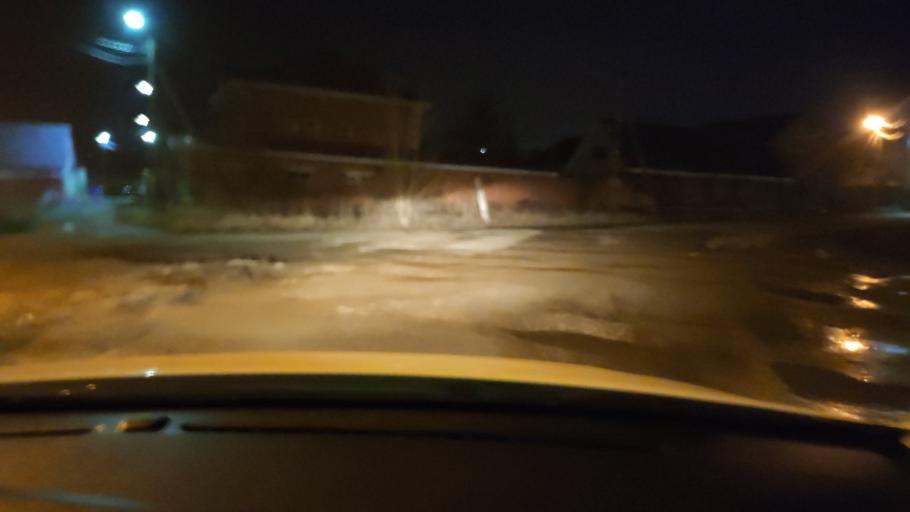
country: RU
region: Tatarstan
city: Vysokaya Gora
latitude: 55.8520
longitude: 49.2369
